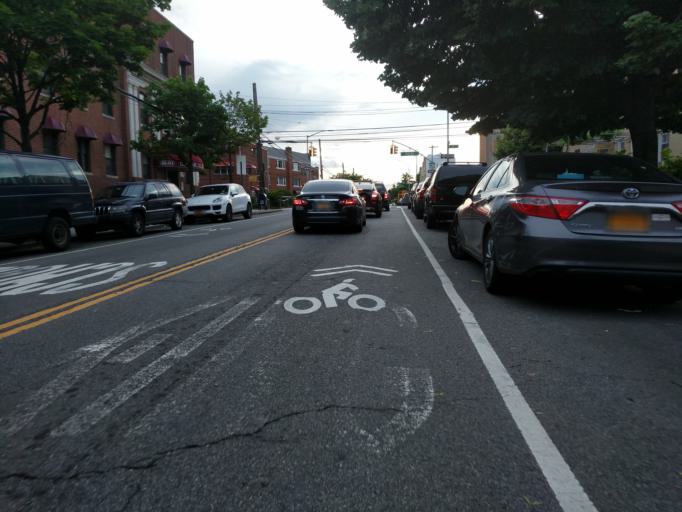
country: US
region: New York
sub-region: Queens County
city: Long Island City
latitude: 40.7594
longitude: -73.9126
